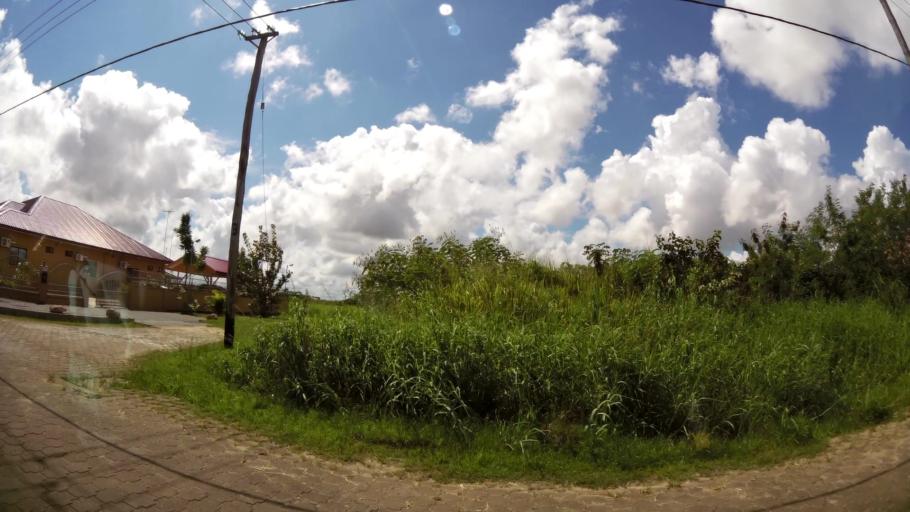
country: SR
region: Paramaribo
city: Paramaribo
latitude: 5.8672
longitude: -55.1300
